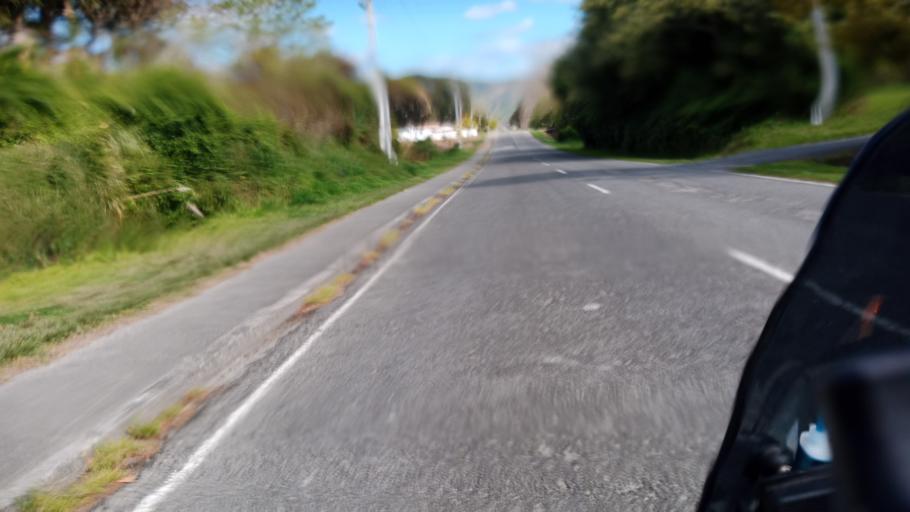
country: NZ
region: Gisborne
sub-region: Gisborne District
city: Gisborne
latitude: -38.6791
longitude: 177.9074
